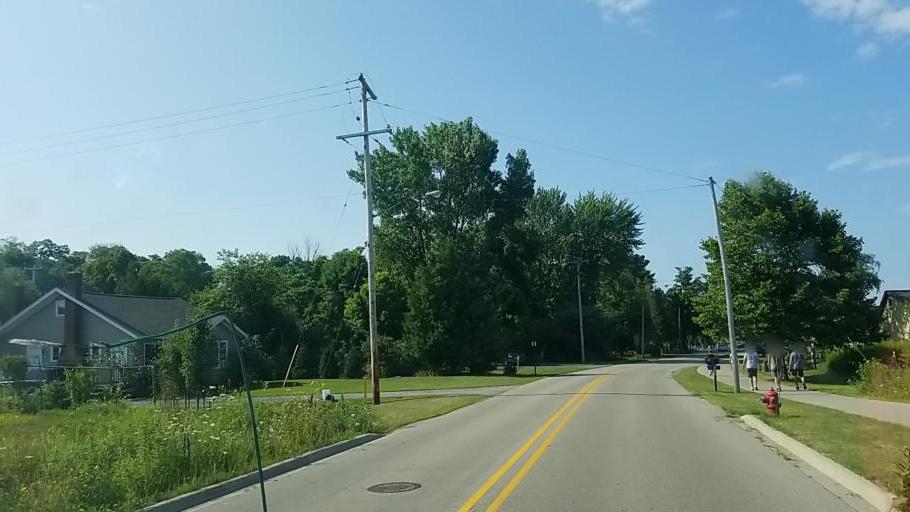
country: US
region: Michigan
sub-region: Muskegon County
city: Whitehall
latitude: 43.3968
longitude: -86.3527
